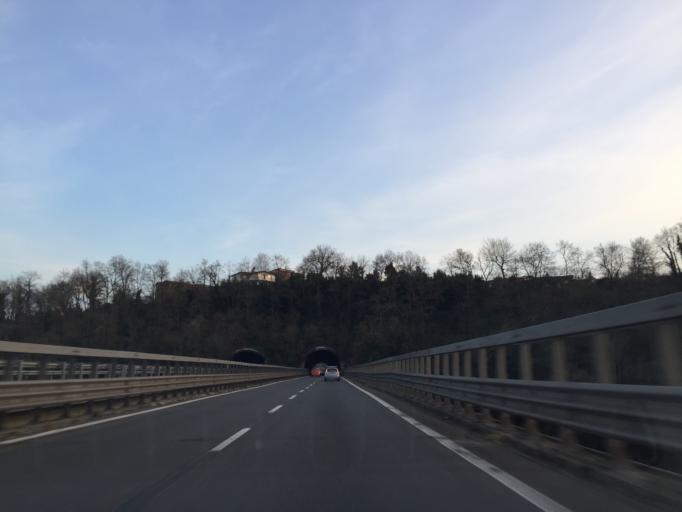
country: IT
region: Latium
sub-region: Citta metropolitana di Roma Capitale
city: Formello
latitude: 42.0152
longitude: 12.4361
